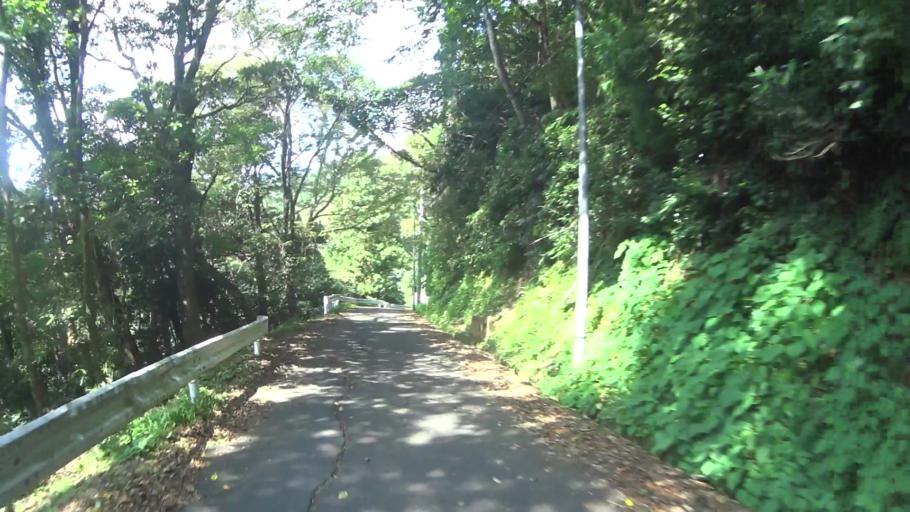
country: JP
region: Kyoto
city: Miyazu
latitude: 35.7401
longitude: 135.1865
